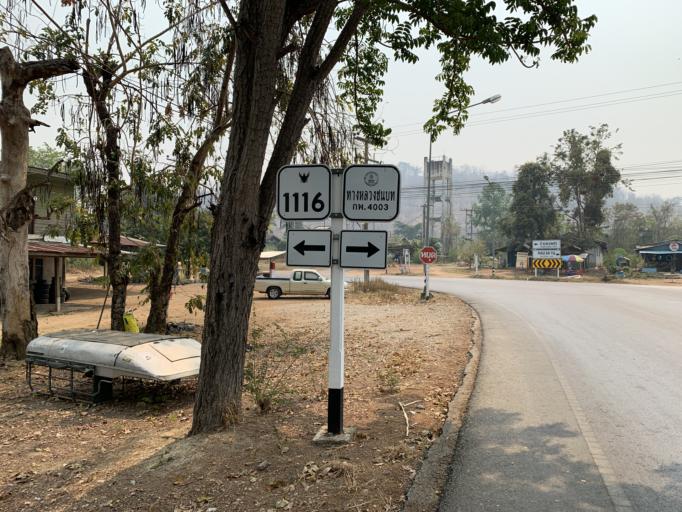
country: TH
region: Kamphaeng Phet
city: Kamphaeng Phet
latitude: 16.4192
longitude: 99.3873
